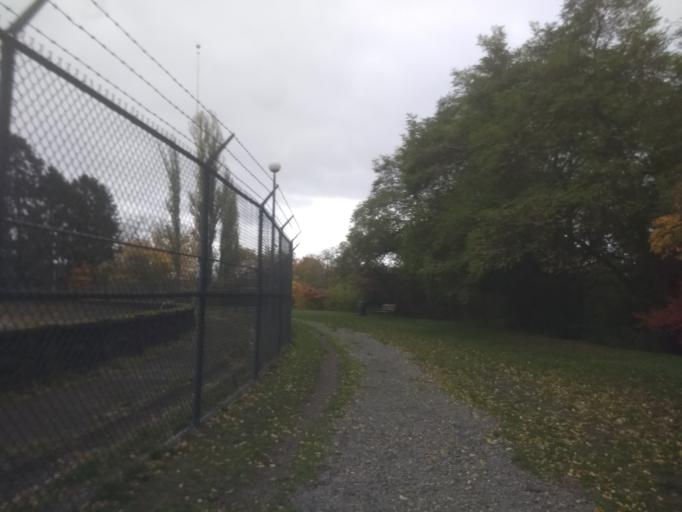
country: US
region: Washington
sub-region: King County
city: Seattle
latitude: 47.6297
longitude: -122.3176
